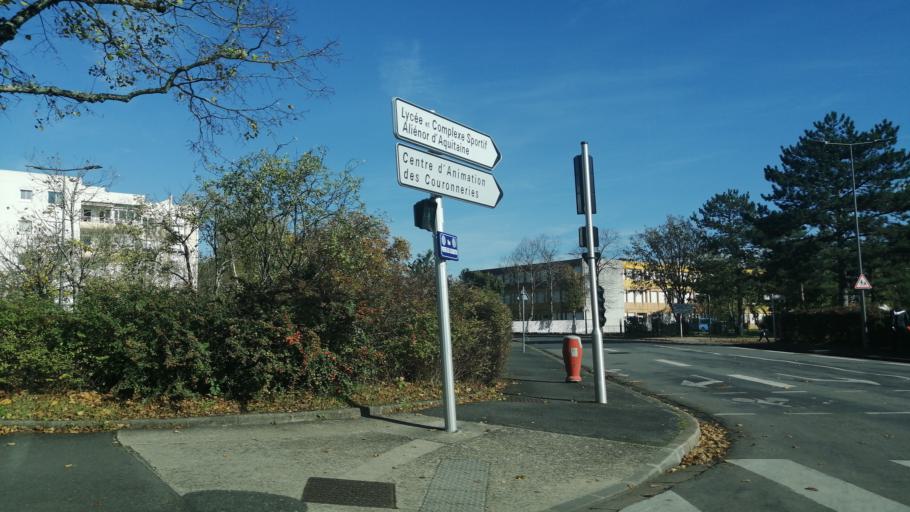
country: FR
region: Poitou-Charentes
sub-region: Departement de la Vienne
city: Poitiers
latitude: 46.5877
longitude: 0.3645
